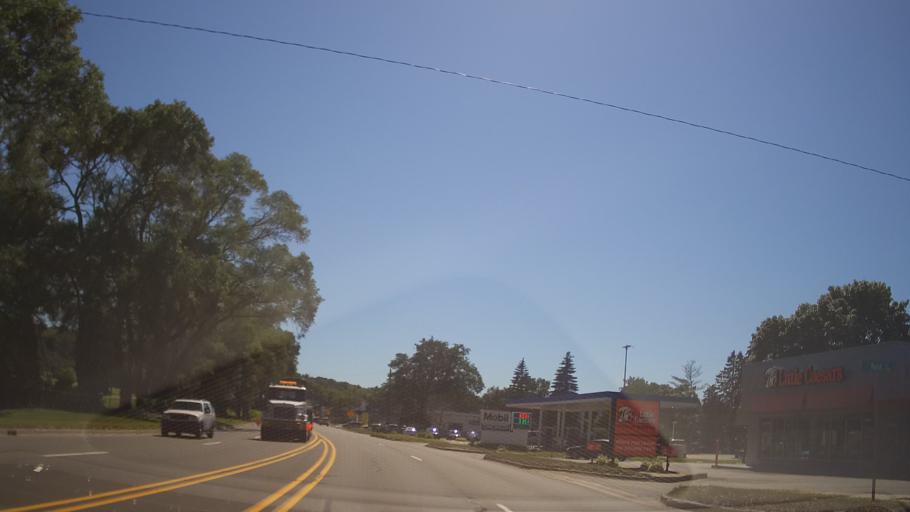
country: US
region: Michigan
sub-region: Emmet County
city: Petoskey
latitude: 45.3891
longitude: -84.9201
